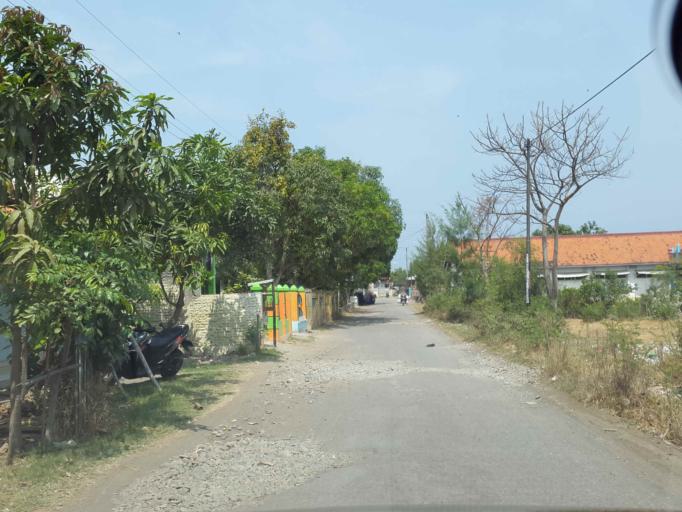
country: ID
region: Central Java
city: Dukuhturi
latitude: -6.8367
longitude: 109.0623
